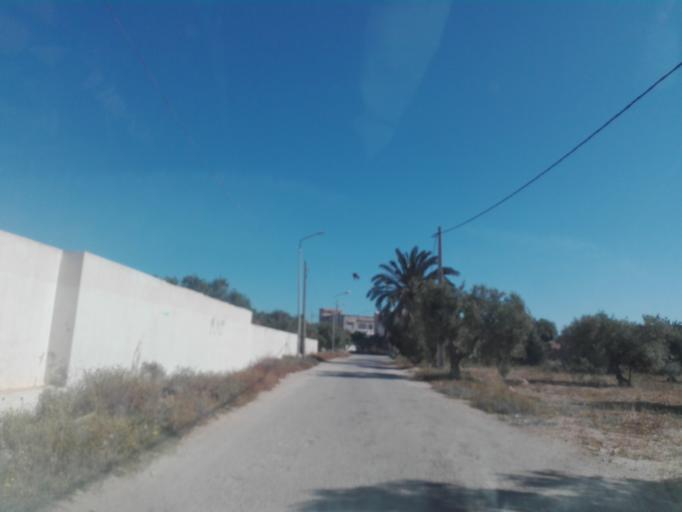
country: TN
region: Safaqis
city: Al Qarmadah
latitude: 34.7097
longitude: 11.2027
